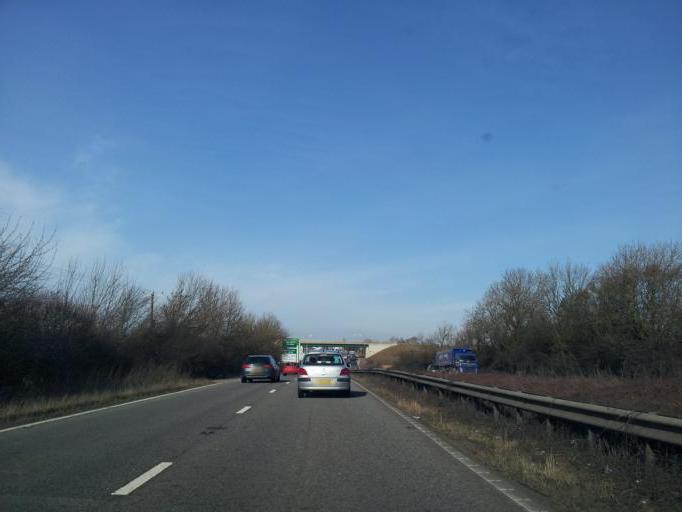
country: GB
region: England
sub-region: District of Rutland
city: Clipsham
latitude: 52.7985
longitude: -0.6107
